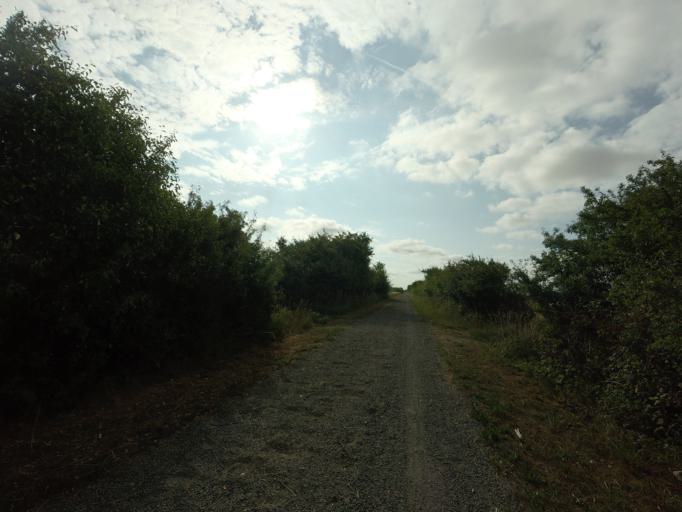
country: SE
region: Skane
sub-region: Helsingborg
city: Odakra
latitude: 56.1632
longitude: 12.7384
